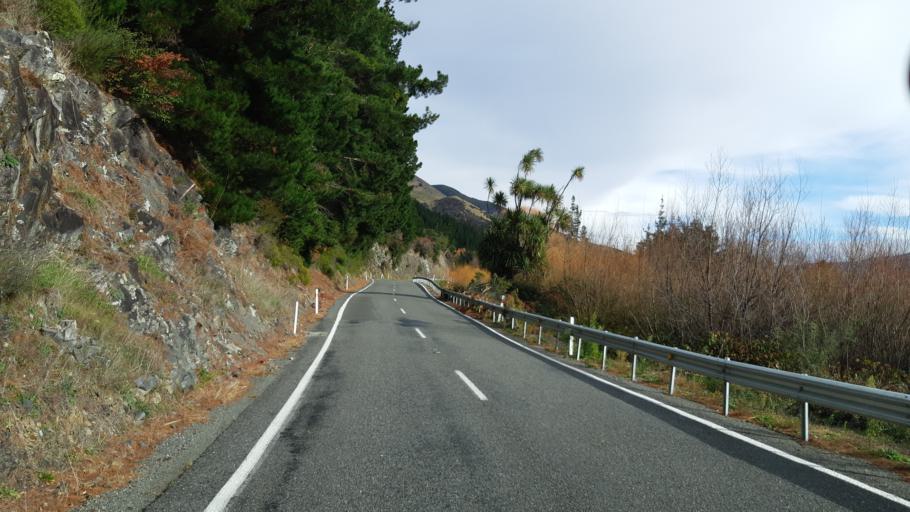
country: NZ
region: Tasman
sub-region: Tasman District
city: Wakefield
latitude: -41.7145
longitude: 173.1102
